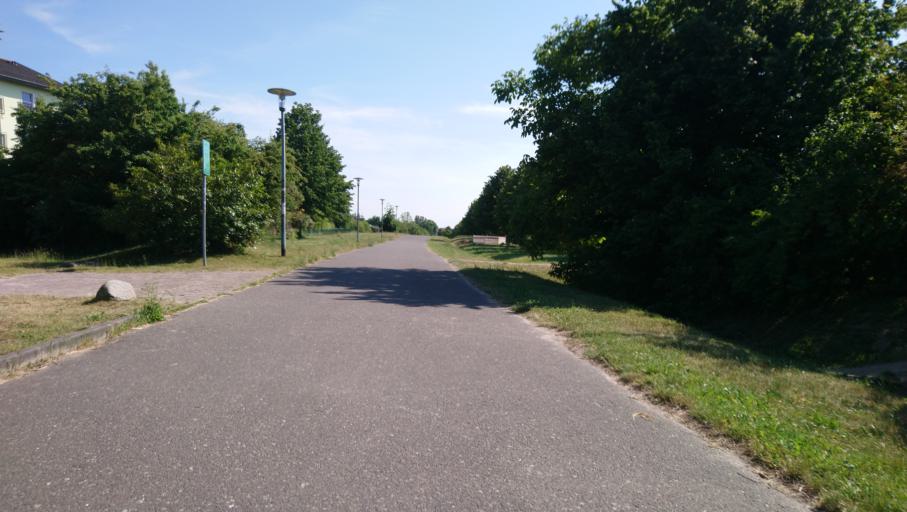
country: DE
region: Mecklenburg-Vorpommern
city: Roggentin
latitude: 54.0871
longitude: 12.1865
